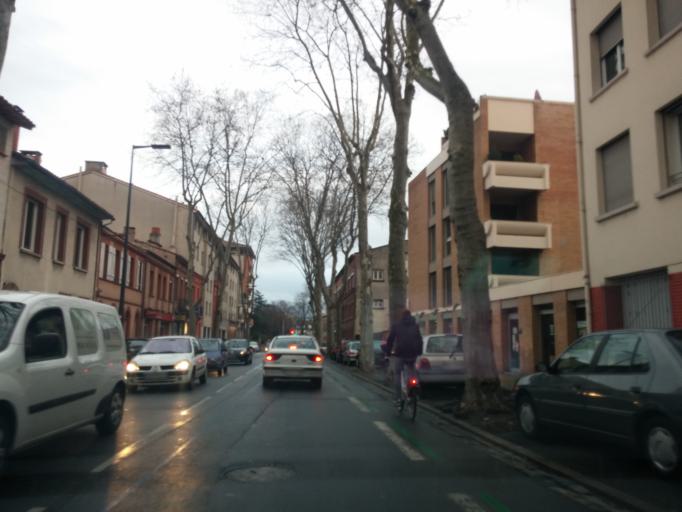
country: FR
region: Midi-Pyrenees
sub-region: Departement de la Haute-Garonne
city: Toulouse
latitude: 43.5841
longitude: 1.4459
